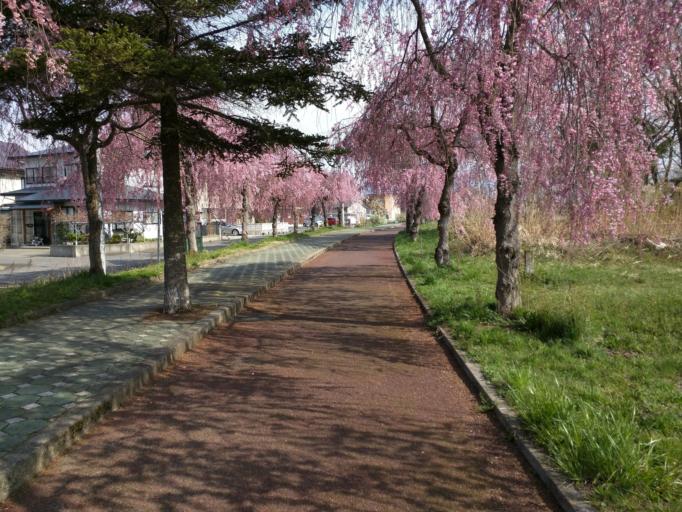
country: JP
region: Fukushima
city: Kitakata
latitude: 37.6470
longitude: 139.8622
